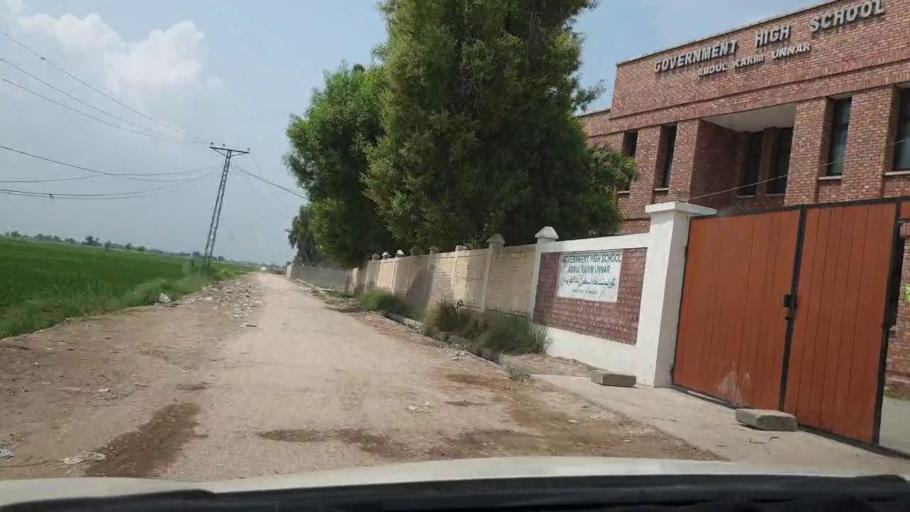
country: PK
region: Sindh
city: Dokri
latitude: 27.3885
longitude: 68.0602
